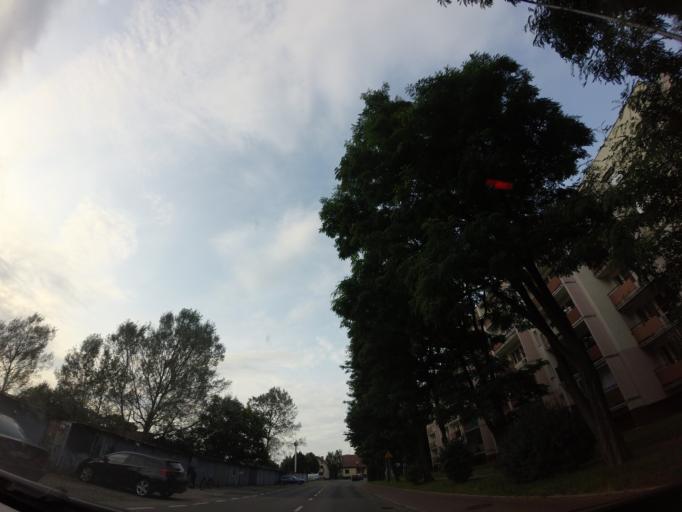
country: PL
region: West Pomeranian Voivodeship
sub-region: Powiat stargardzki
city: Stargard Szczecinski
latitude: 53.3405
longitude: 15.0031
